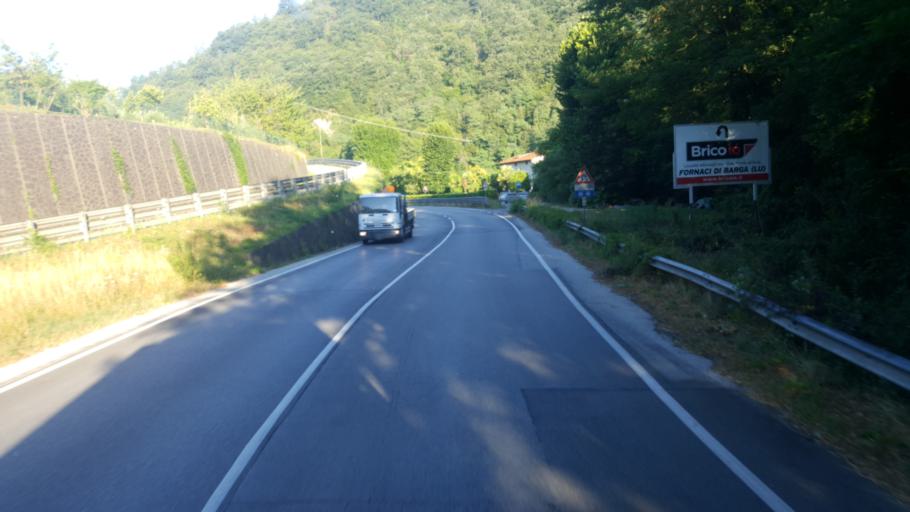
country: IT
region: Tuscany
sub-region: Provincia di Lucca
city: Fosciandora
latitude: 44.1161
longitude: 10.4380
